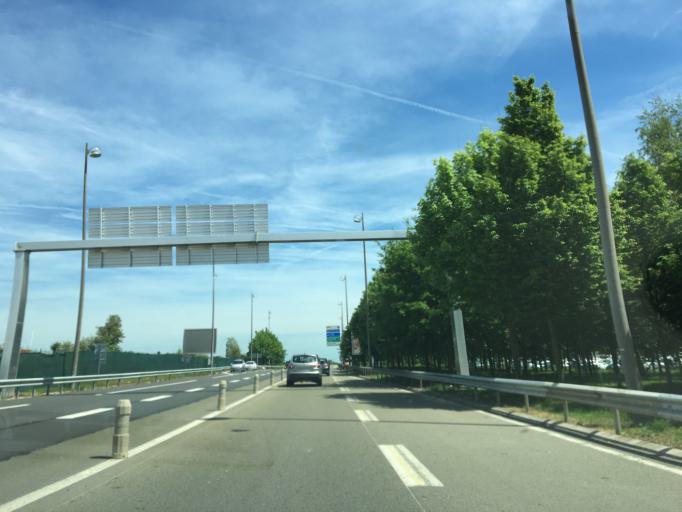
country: FR
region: Ile-de-France
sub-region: Departement de Seine-et-Marne
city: Mitry-Mory
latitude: 49.0088
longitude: 2.6057
